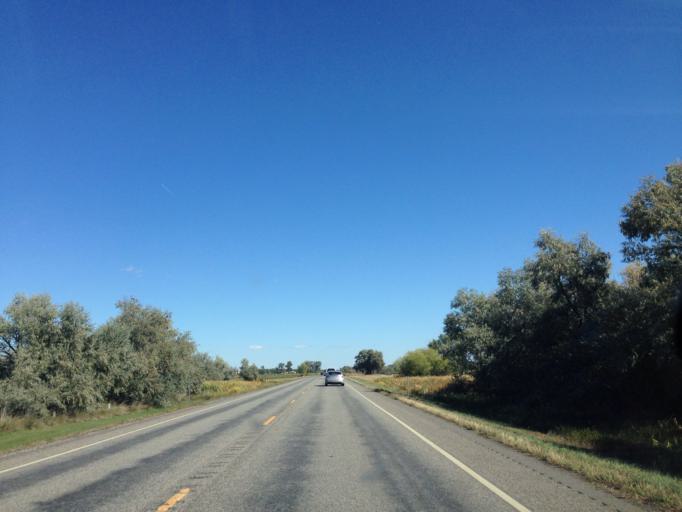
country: US
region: Montana
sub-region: Yellowstone County
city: Laurel
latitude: 45.5938
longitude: -108.8136
